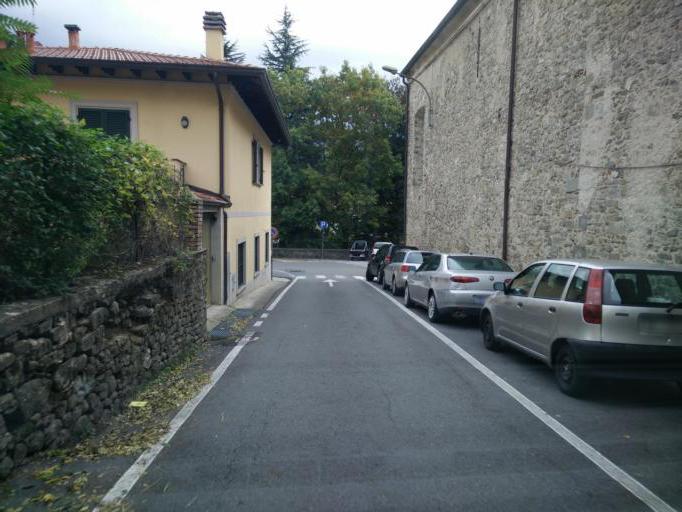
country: IT
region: Tuscany
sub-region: Provincia di Massa-Carrara
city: Pontremoli
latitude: 44.3756
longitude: 9.8814
